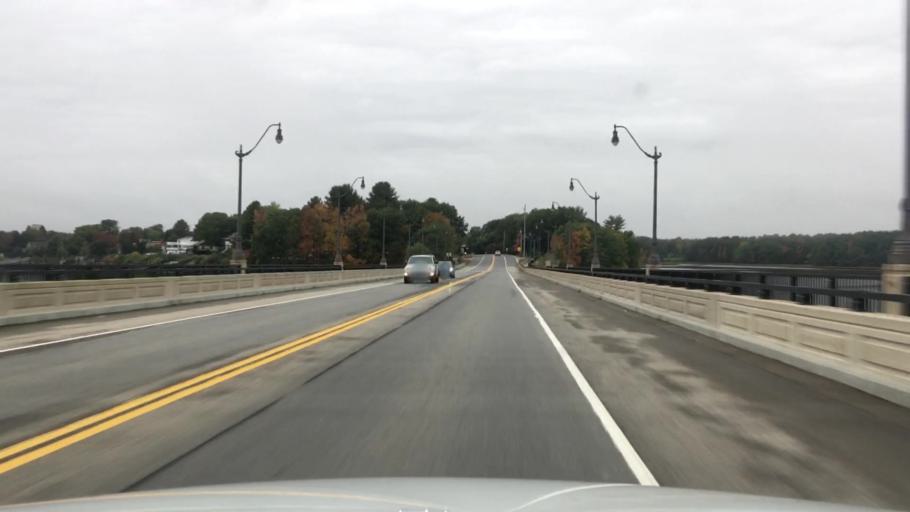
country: US
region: Maine
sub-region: York County
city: Eliot
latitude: 43.1294
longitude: -70.8493
